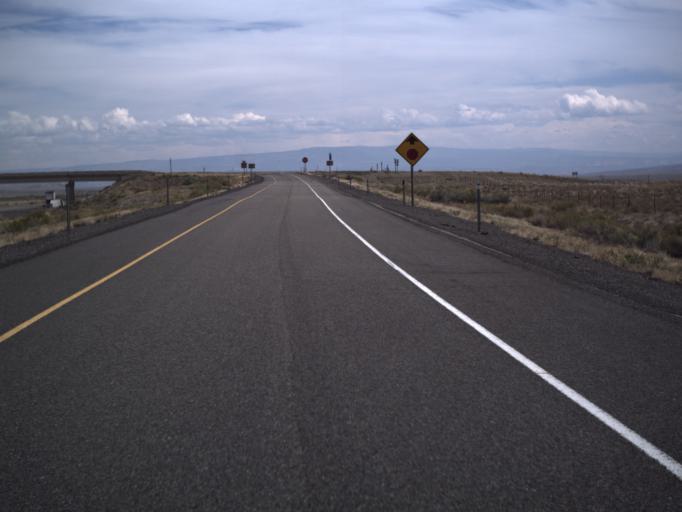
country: US
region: Utah
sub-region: Grand County
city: Moab
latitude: 38.9417
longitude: -109.6184
